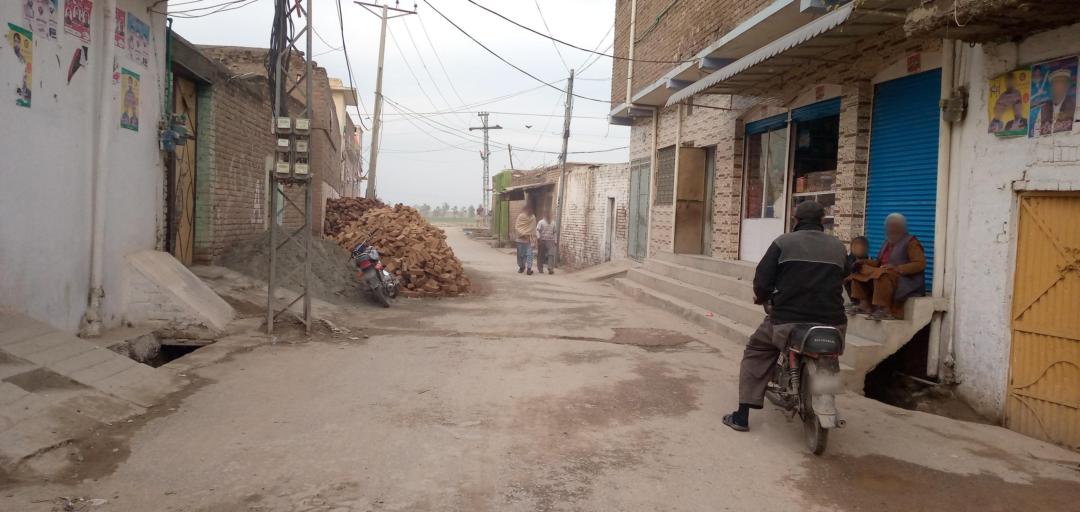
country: PK
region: Khyber Pakhtunkhwa
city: Peshawar
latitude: 34.0159
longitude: 71.5029
